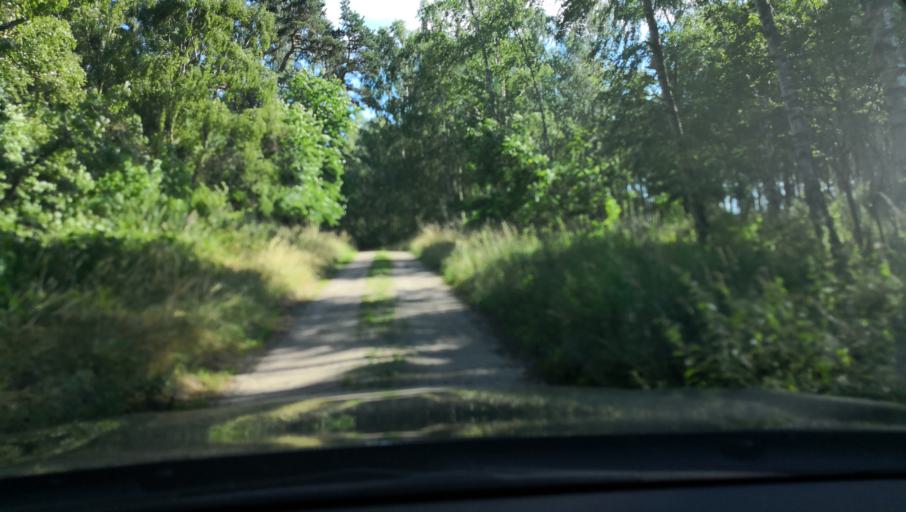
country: SE
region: Skane
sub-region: Kristianstads Kommun
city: Degeberga
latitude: 55.7986
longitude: 14.1955
